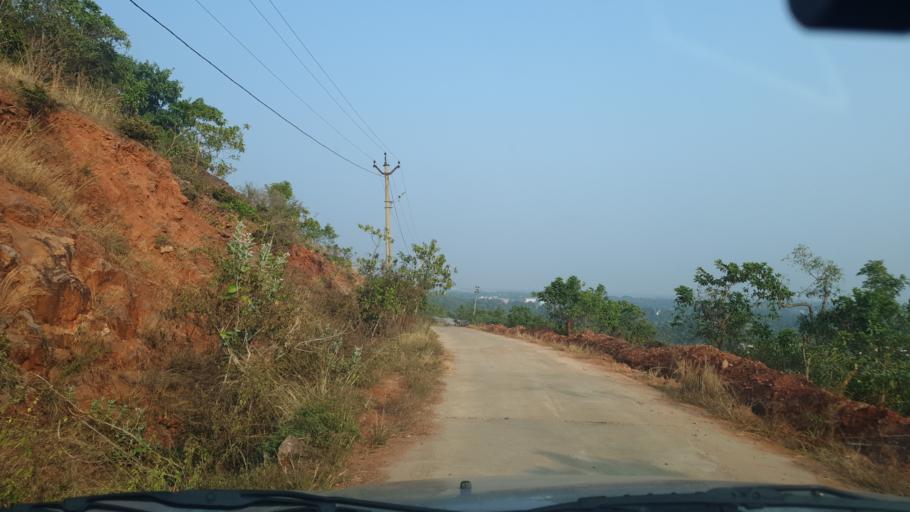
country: IN
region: Andhra Pradesh
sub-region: Srikakulam
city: Narasannapeta
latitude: 18.3316
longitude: 84.0349
